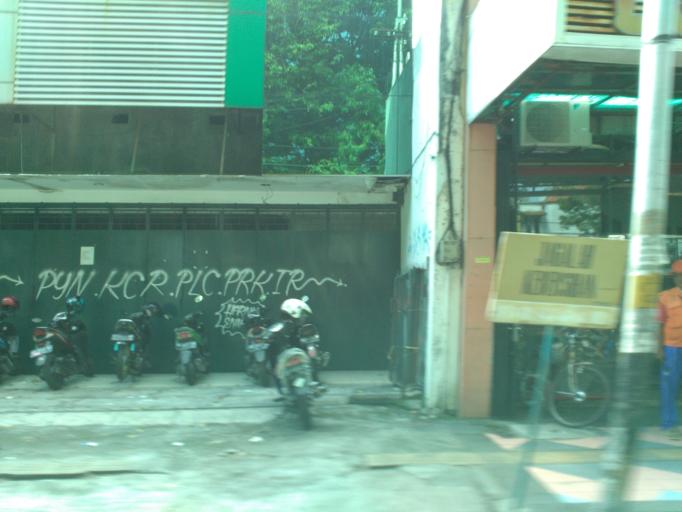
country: ID
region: Central Java
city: Klaten
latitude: -7.7011
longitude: 110.6043
